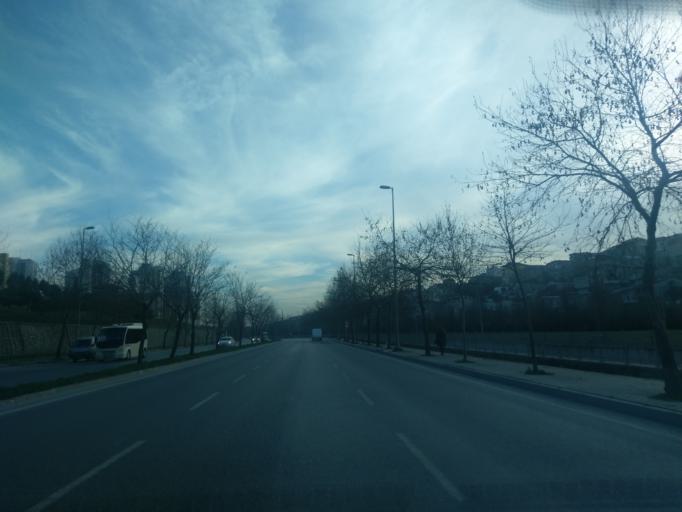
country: TR
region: Istanbul
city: Basaksehir
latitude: 41.0553
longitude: 28.7574
